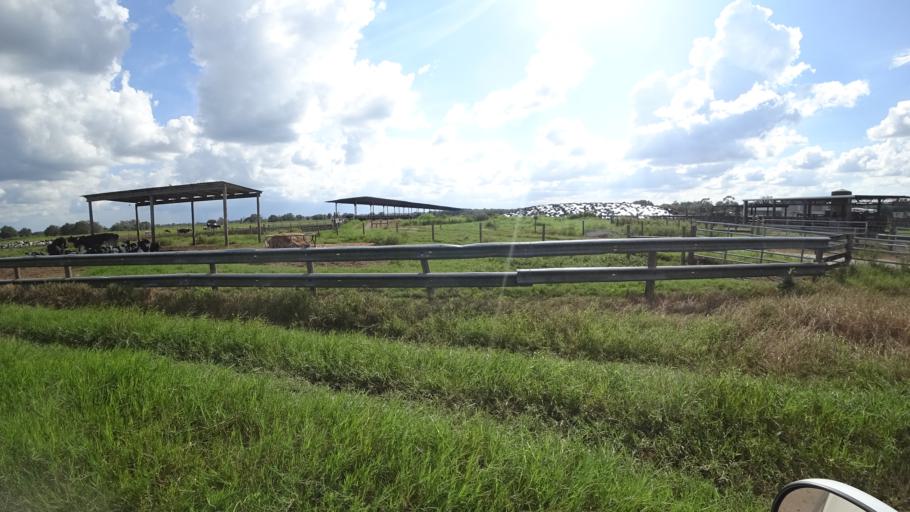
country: US
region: Florida
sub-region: DeSoto County
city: Nocatee
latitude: 27.2903
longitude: -82.1107
